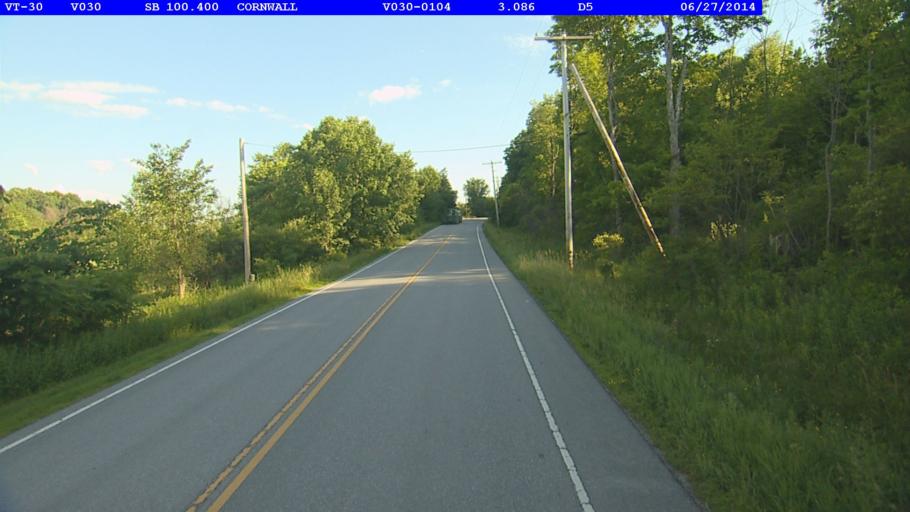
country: US
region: Vermont
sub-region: Addison County
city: Middlebury (village)
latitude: 43.9521
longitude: -73.2102
